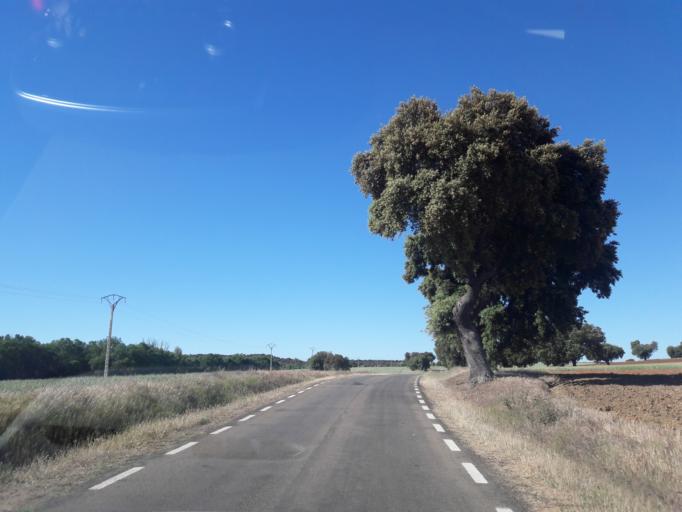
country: ES
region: Castille and Leon
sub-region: Provincia de Salamanca
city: Florida de Liebana
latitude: 41.0150
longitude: -5.7684
